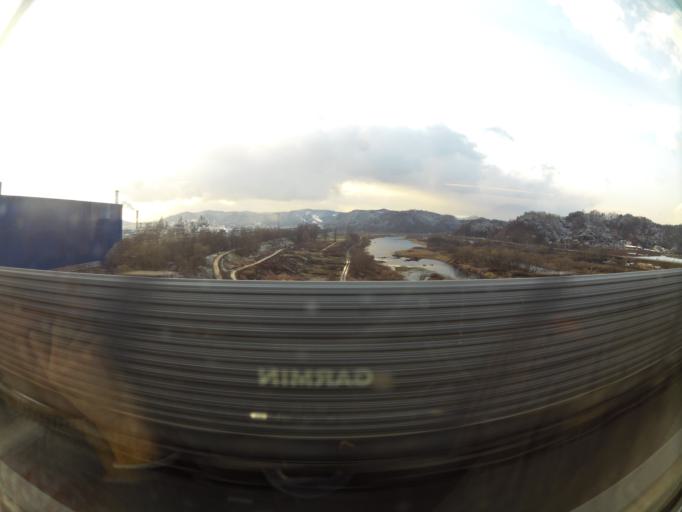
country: KR
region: Daejeon
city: Sintansin
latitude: 36.4536
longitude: 127.4165
